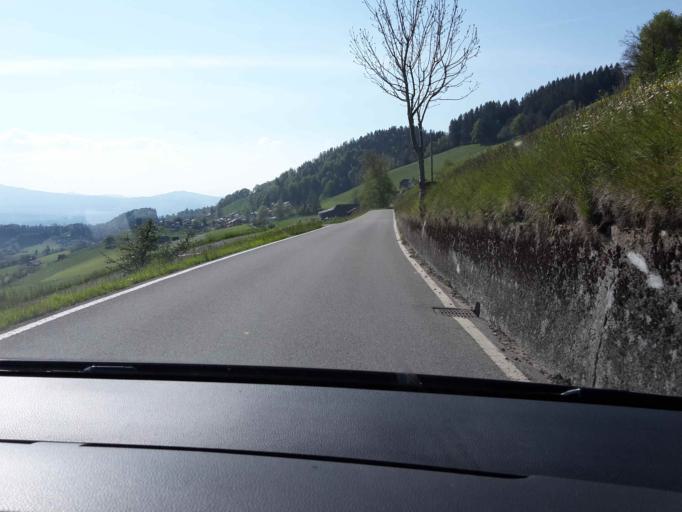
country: CH
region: Bern
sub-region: Thun District
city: Hilterfingen
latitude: 46.7608
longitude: 7.6906
